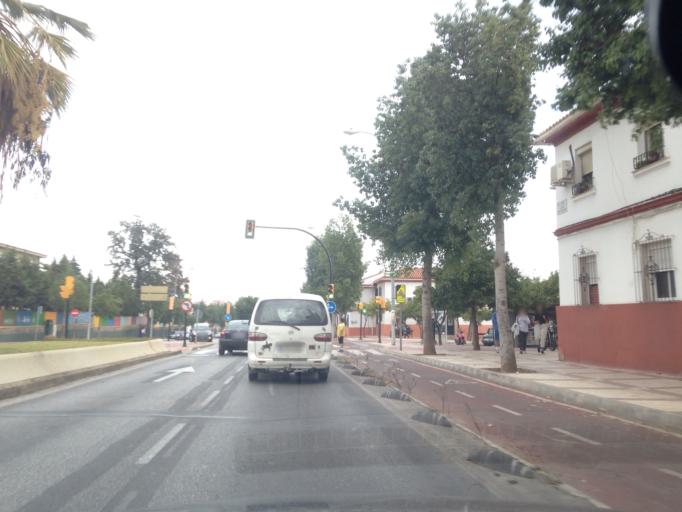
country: ES
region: Andalusia
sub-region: Provincia de Malaga
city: Malaga
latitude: 36.7189
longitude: -4.4470
